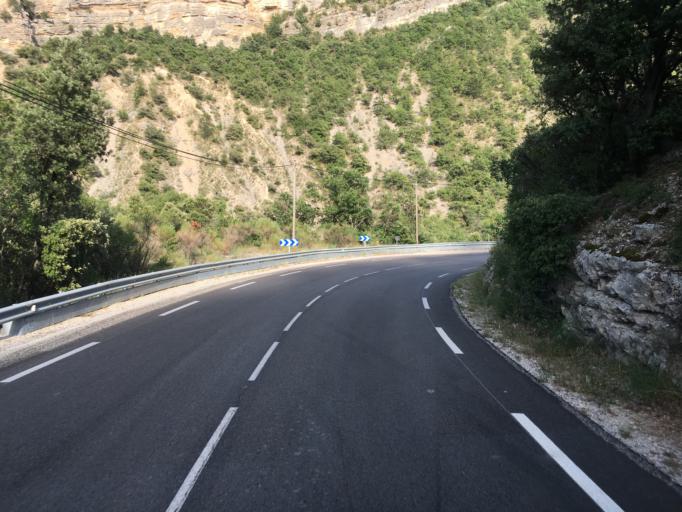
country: FR
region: Rhone-Alpes
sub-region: Departement de la Drome
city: Buis-les-Baronnies
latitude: 44.4282
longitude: 5.2791
